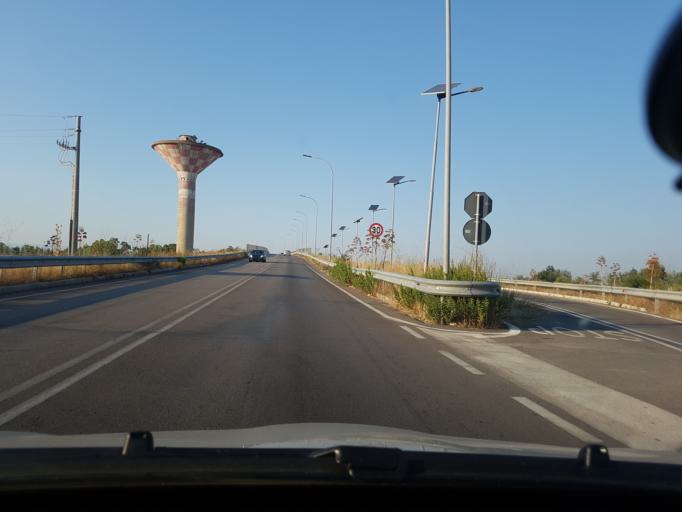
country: IT
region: Apulia
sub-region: Provincia di Foggia
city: Carapelle
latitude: 41.4042
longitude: 15.6513
